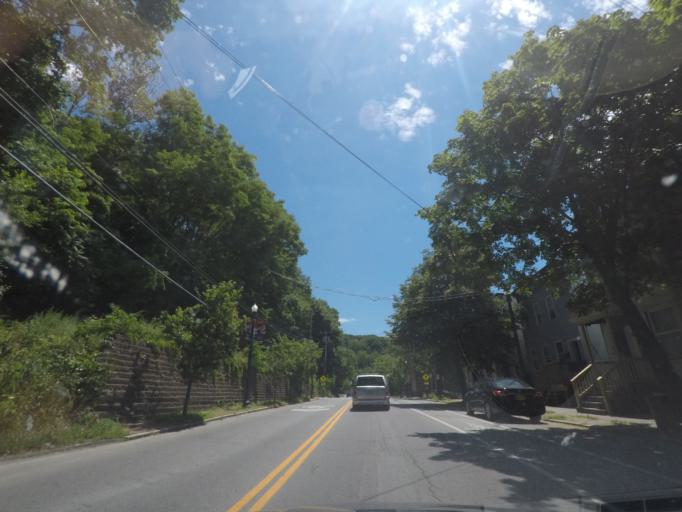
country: US
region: New York
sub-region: Rensselaer County
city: Troy
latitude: 42.7057
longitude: -73.6976
